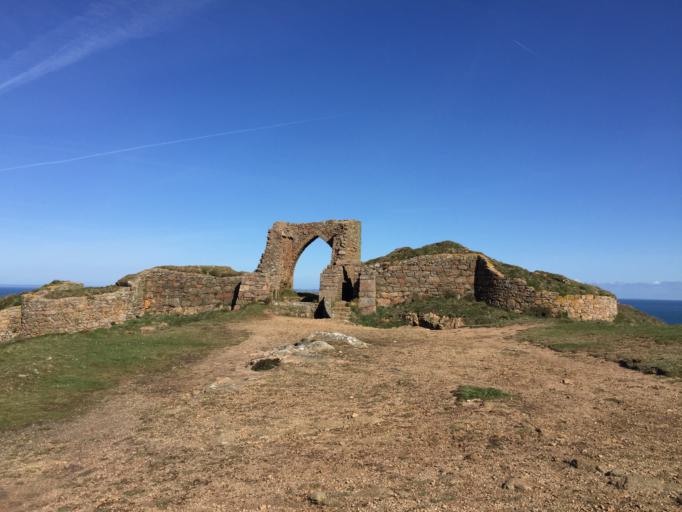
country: JE
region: St Helier
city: Saint Helier
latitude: 49.2570
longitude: -2.2462
